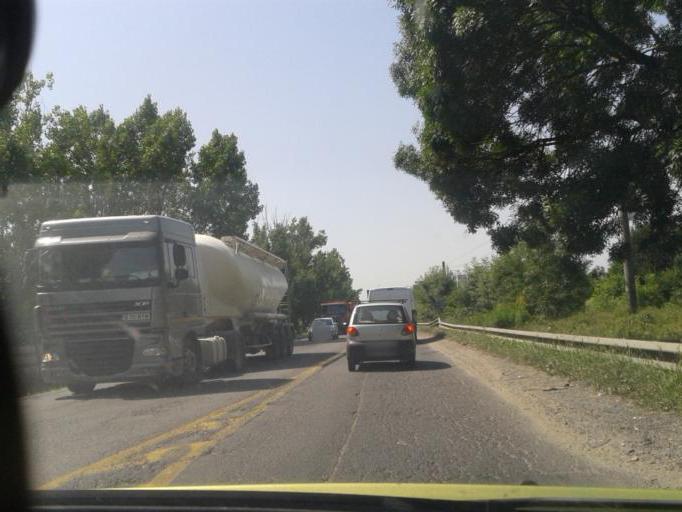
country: RO
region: Ilfov
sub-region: Comuna Pantelimon
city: Pantelimon
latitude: 44.4505
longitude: 26.2359
